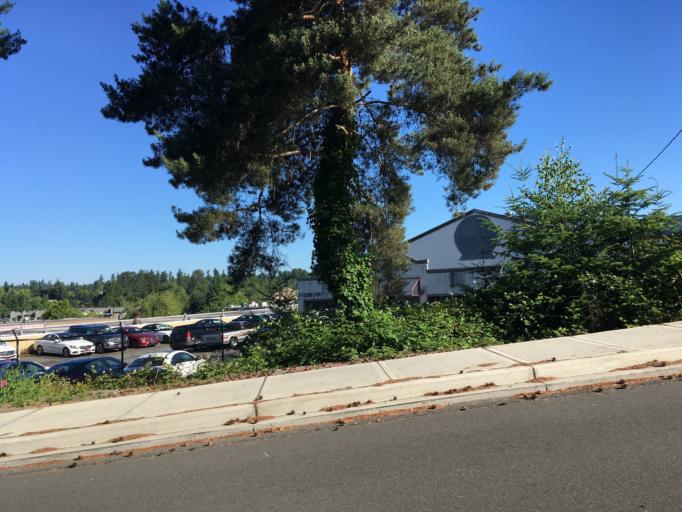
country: US
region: Washington
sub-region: King County
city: Bellevue
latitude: 47.6189
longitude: -122.1777
